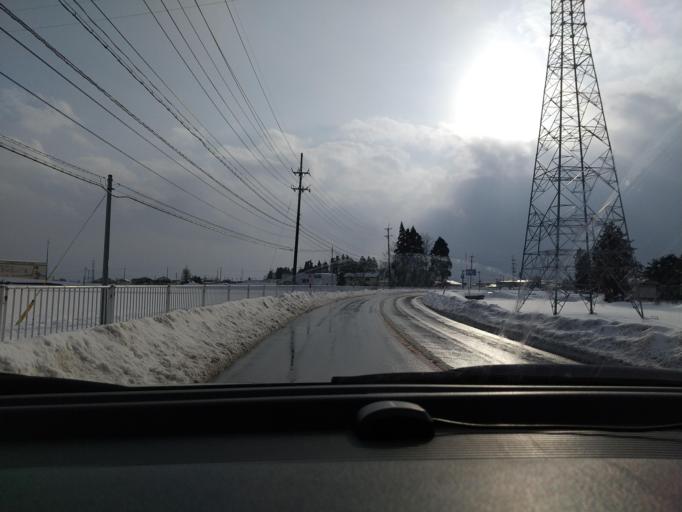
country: JP
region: Akita
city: Omagari
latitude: 39.5082
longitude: 140.5120
